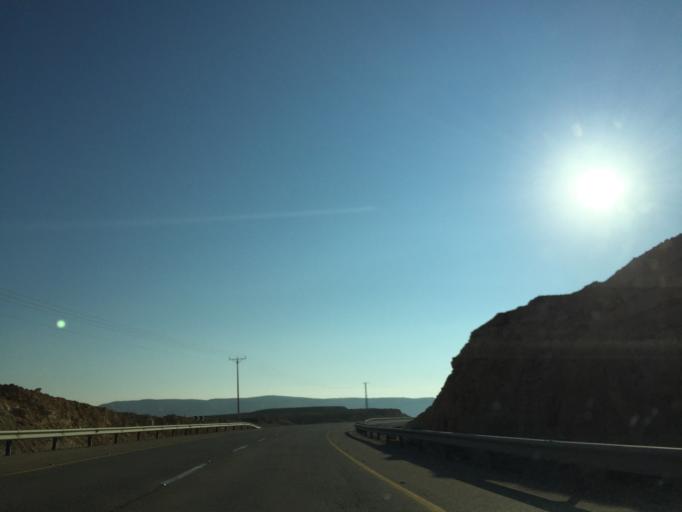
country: IL
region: Southern District
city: Mitzpe Ramon
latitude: 30.2893
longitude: 34.9942
